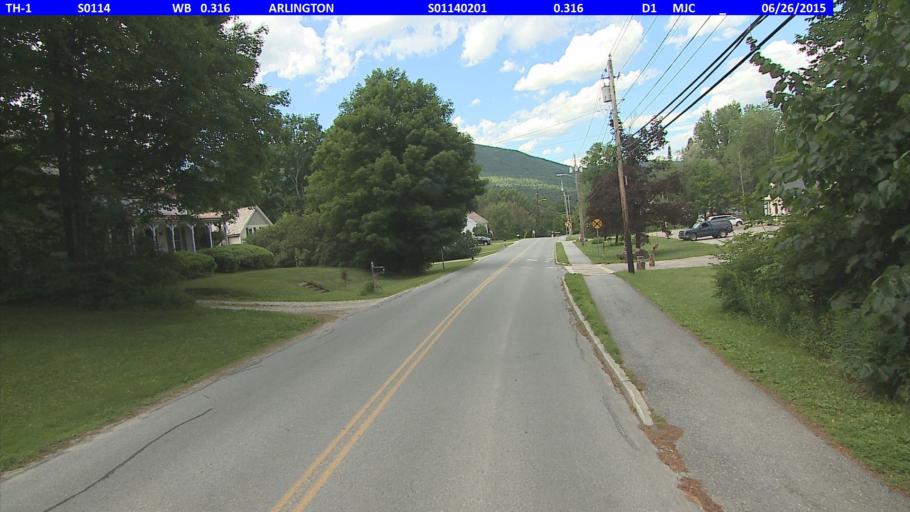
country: US
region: Vermont
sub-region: Bennington County
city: Arlington
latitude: 43.0686
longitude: -73.1535
